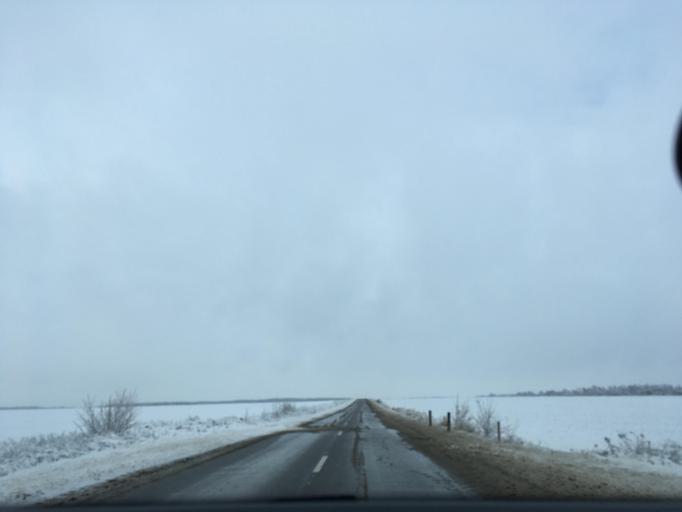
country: RU
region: Voronezj
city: Ol'khovatka
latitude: 50.1373
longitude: 39.2027
